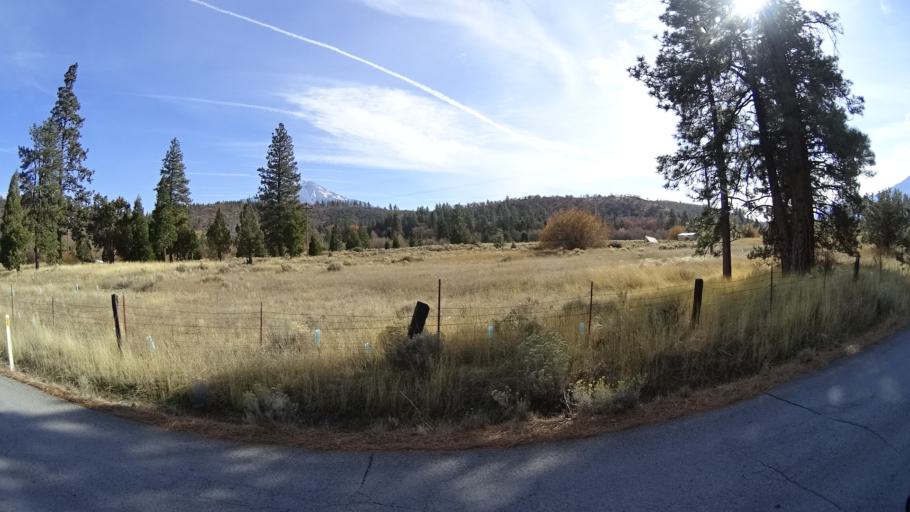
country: US
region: California
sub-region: Siskiyou County
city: Weed
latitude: 41.4458
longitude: -122.4340
